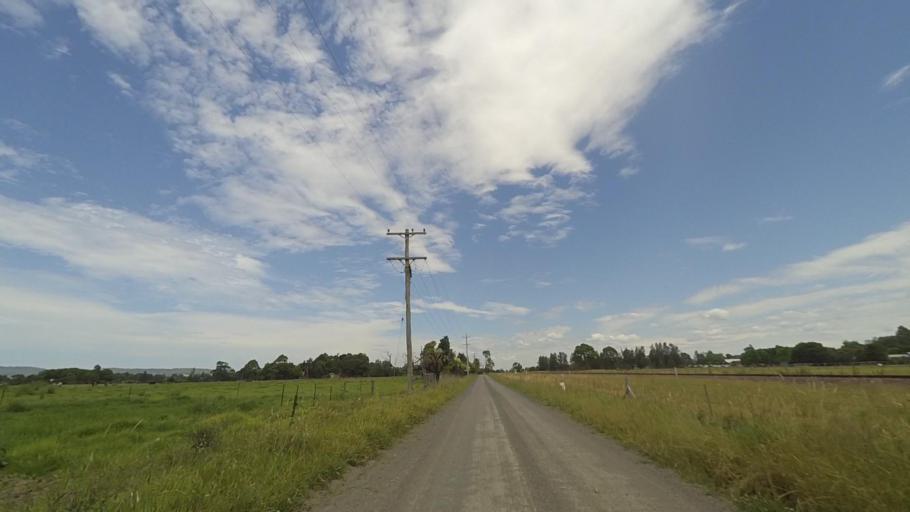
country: AU
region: New South Wales
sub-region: Shoalhaven Shire
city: Berry
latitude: -34.7923
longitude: 150.6782
